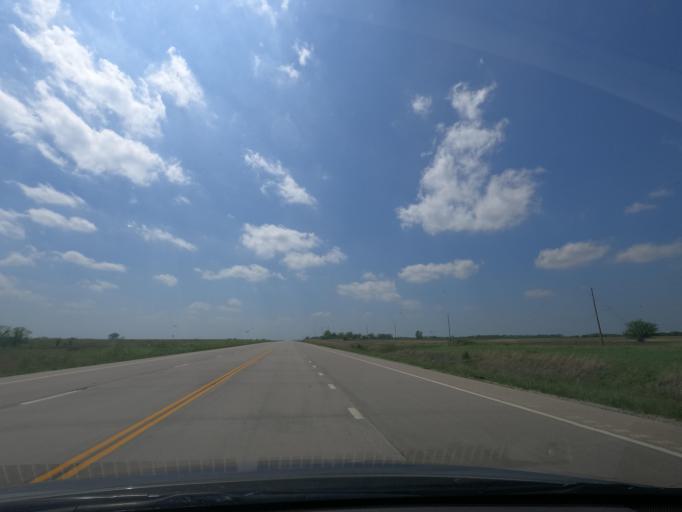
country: US
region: Kansas
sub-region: Elk County
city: Howard
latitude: 37.6347
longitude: -96.1901
